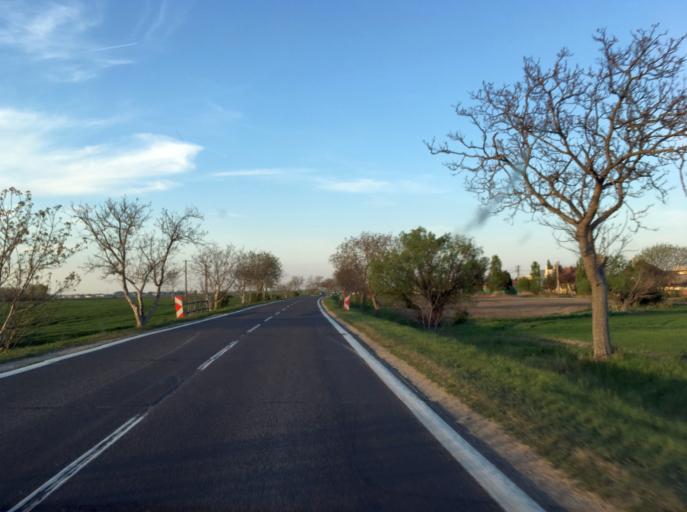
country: SK
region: Trnavsky
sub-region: Okres Dunajska Streda
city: Velky Meder
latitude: 47.8492
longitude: 17.7345
